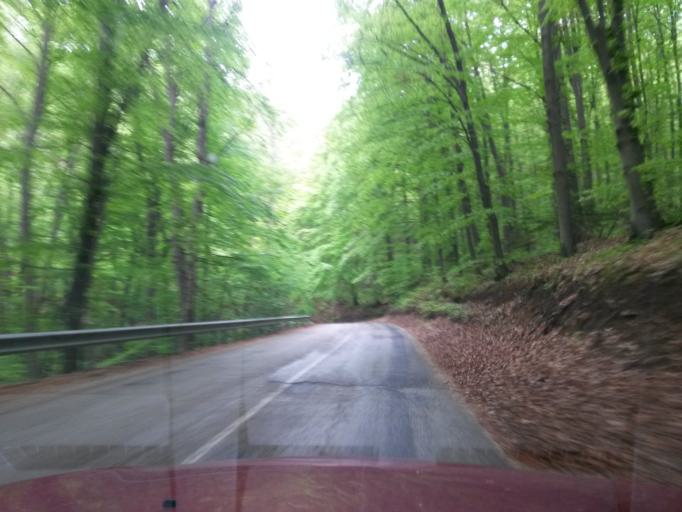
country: SK
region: Kosicky
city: Roznava
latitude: 48.5626
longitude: 20.4745
